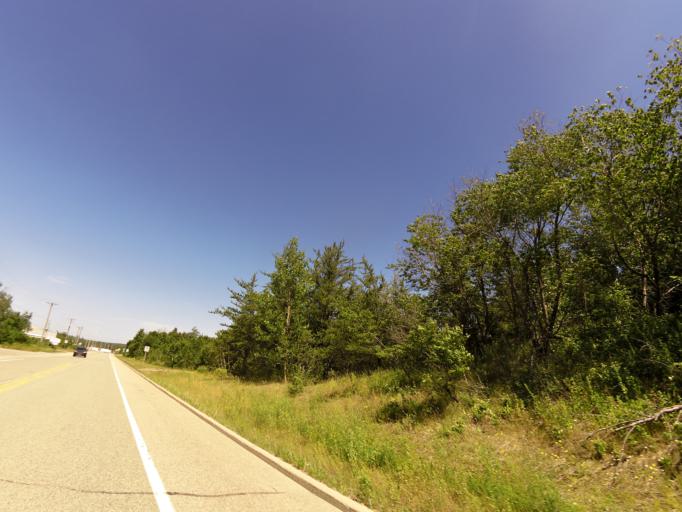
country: CA
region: Quebec
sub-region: Abitibi-Temiscamingue
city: Temiscaming
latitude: 46.7348
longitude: -79.0636
